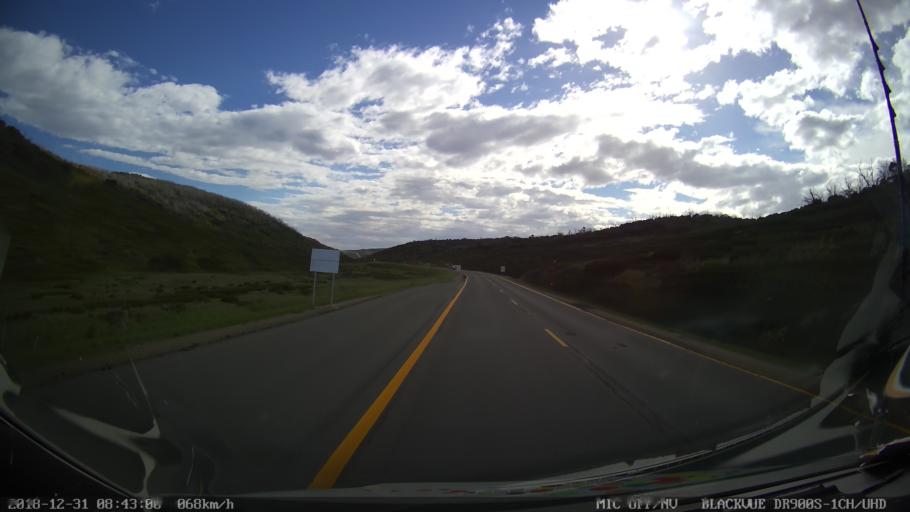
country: AU
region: New South Wales
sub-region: Snowy River
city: Jindabyne
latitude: -36.3915
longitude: 148.4395
